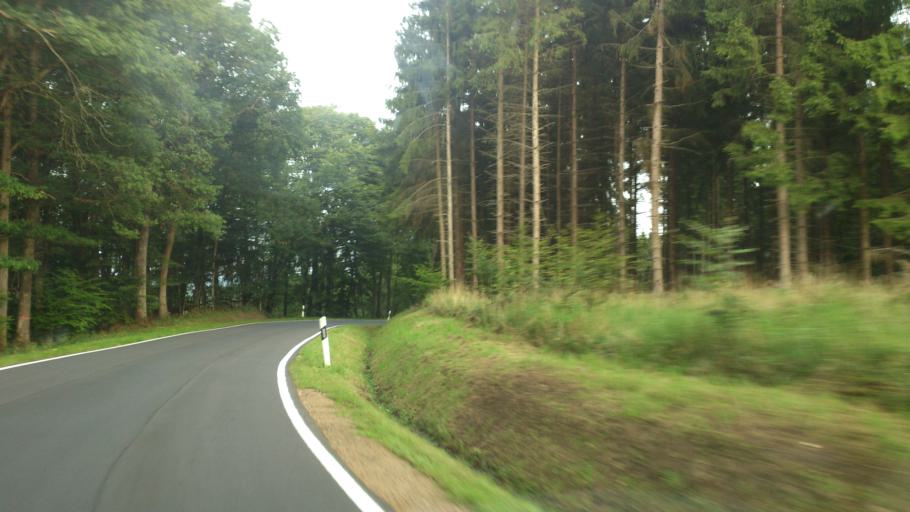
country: DE
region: Rheinland-Pfalz
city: Bongard
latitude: 50.3041
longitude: 6.8108
